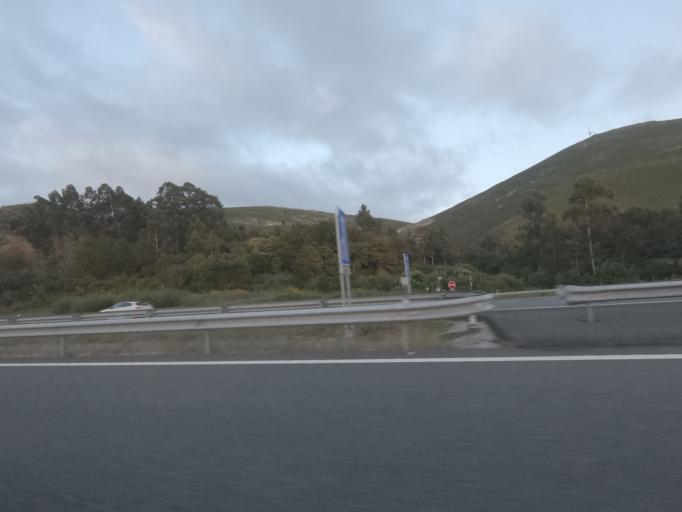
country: ES
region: Galicia
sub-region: Provincia de Pontevedra
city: Covelo
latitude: 42.1715
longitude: -8.3764
